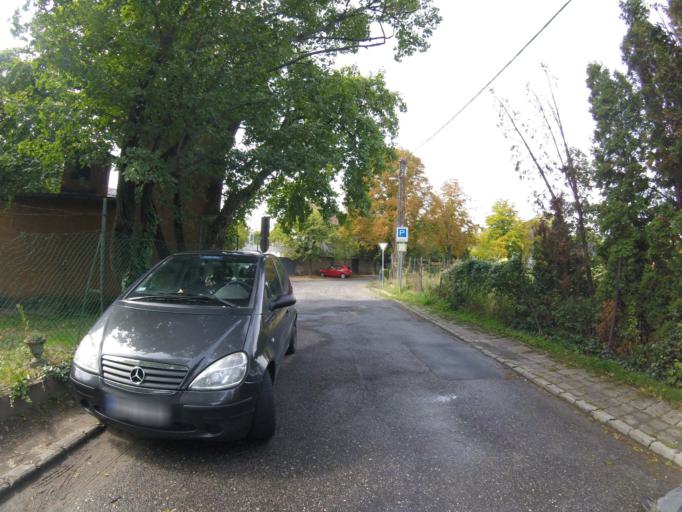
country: HU
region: Pest
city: Szentendre
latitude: 47.6706
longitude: 19.0745
